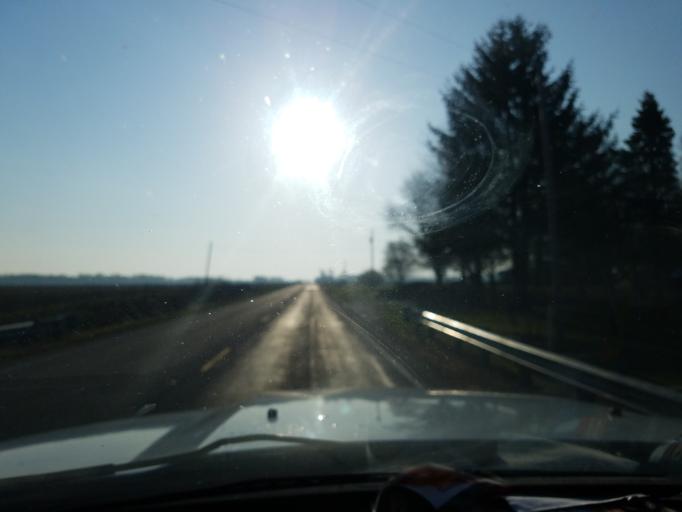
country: US
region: Indiana
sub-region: Vigo County
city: Seelyville
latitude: 39.3890
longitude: -87.1994
